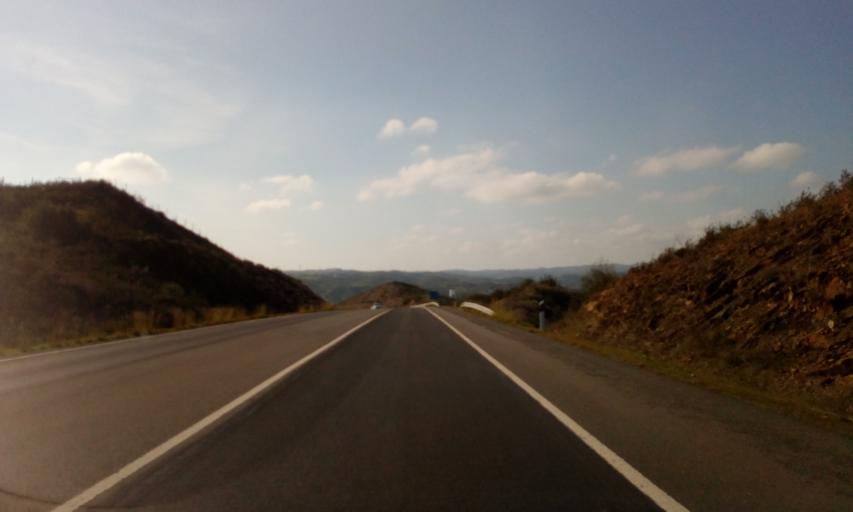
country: PT
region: Faro
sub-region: Castro Marim
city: Castro Marim
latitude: 37.2819
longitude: -7.4912
